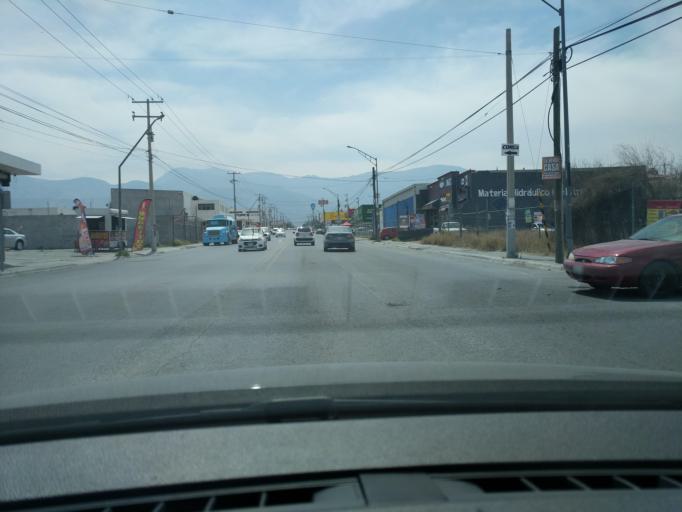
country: MX
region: Coahuila
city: Saltillo
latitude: 25.4270
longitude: -100.9462
